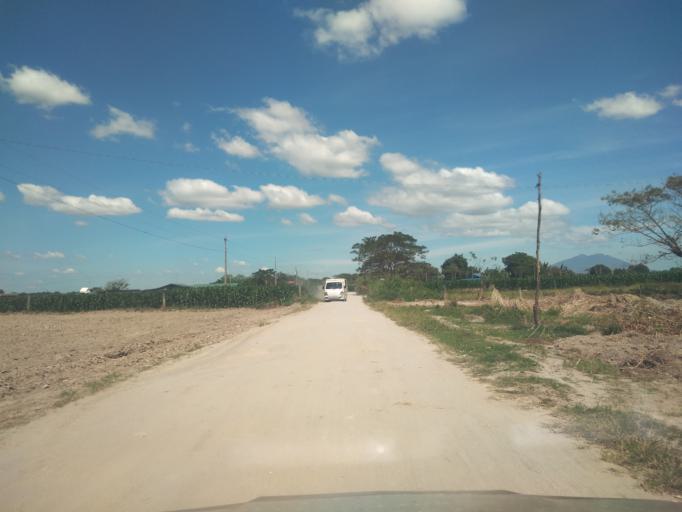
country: PH
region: Central Luzon
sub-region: Province of Pampanga
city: San Basilio
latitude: 15.0266
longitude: 120.6050
